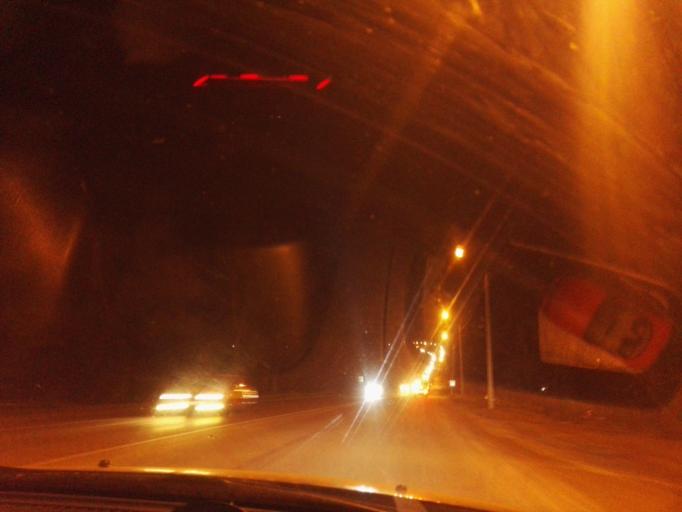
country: RU
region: Tula
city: Skuratovskiy
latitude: 54.1291
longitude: 37.6812
